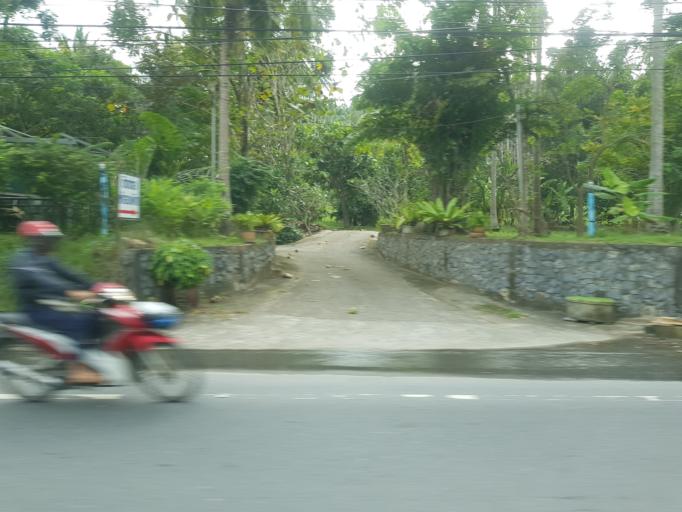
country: TH
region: Surat Thani
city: Ko Samui
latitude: 9.4620
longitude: 99.9786
